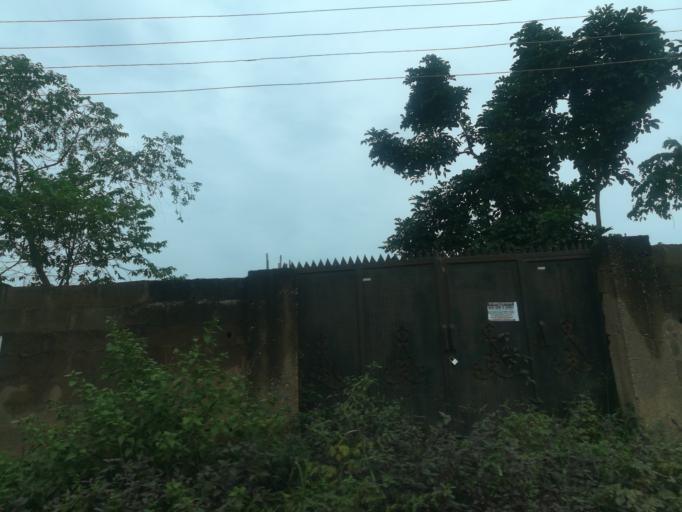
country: NG
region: Oyo
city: Egbeda
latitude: 7.3776
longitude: 3.9957
